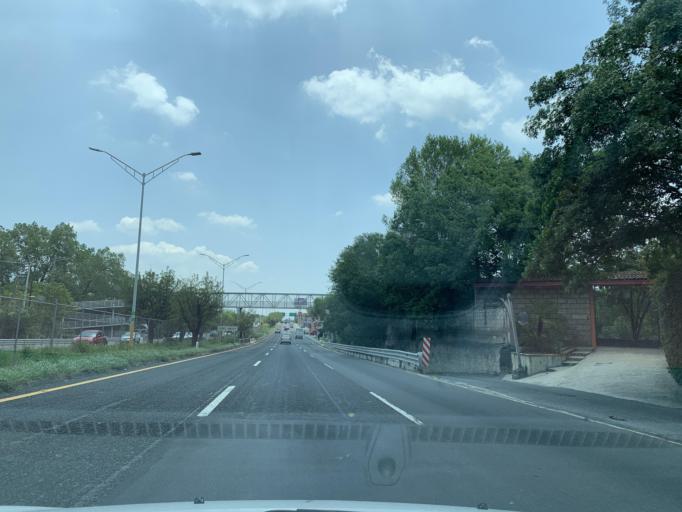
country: MX
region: Nuevo Leon
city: Santiago
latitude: 25.4944
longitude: -100.1878
